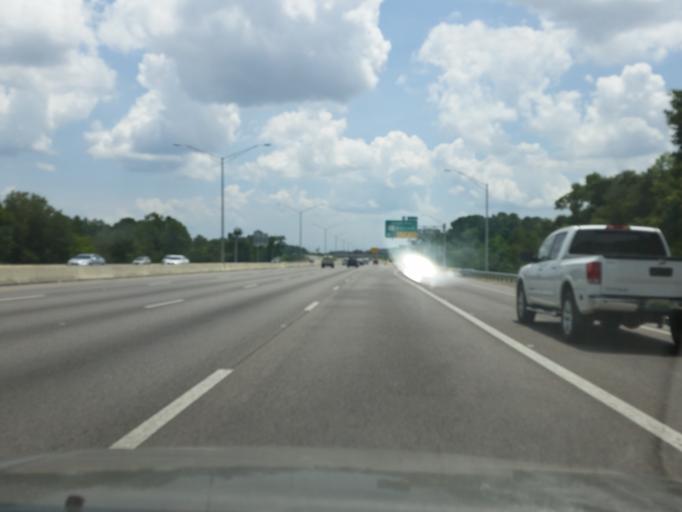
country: US
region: Florida
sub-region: Escambia County
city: Brent
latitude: 30.4907
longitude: -87.2305
